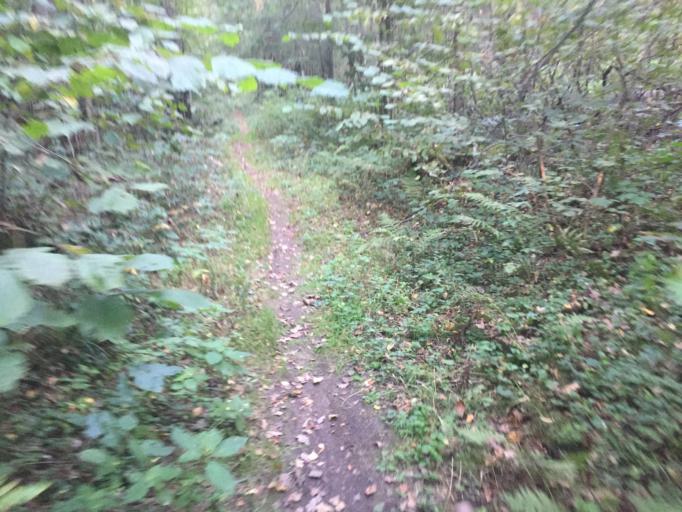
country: RU
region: Moscow
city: Gol'yanovo
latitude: 55.8496
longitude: 37.8089
